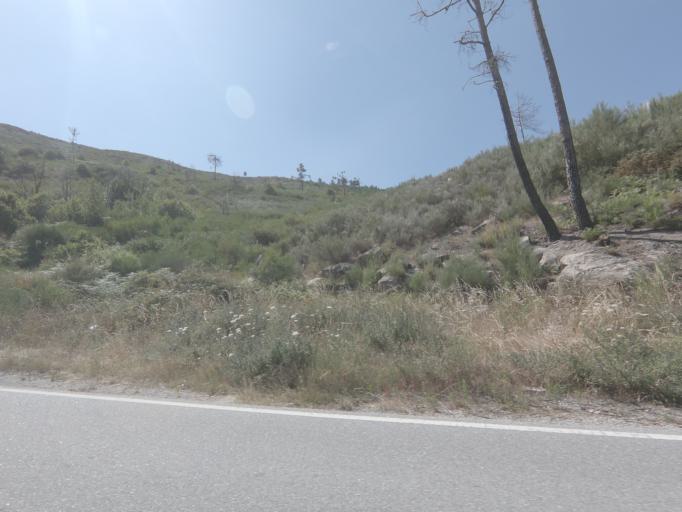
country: PT
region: Viseu
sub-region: Tarouca
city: Tarouca
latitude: 40.9995
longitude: -7.7815
